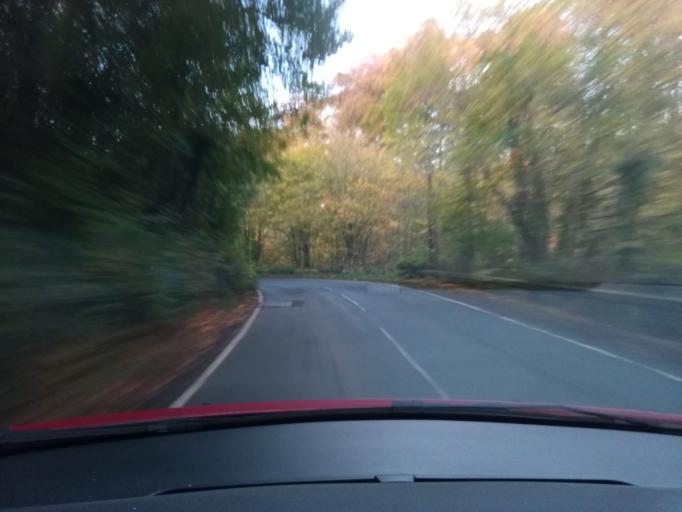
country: GB
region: England
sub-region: Northumberland
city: Bardon Mill
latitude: 54.9638
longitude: -2.2434
